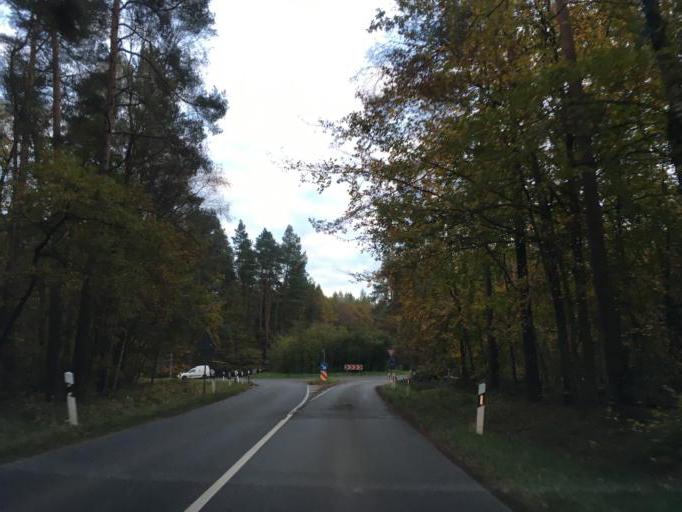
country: DE
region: Lower Saxony
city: Barendorf
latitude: 53.2551
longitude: 10.5263
